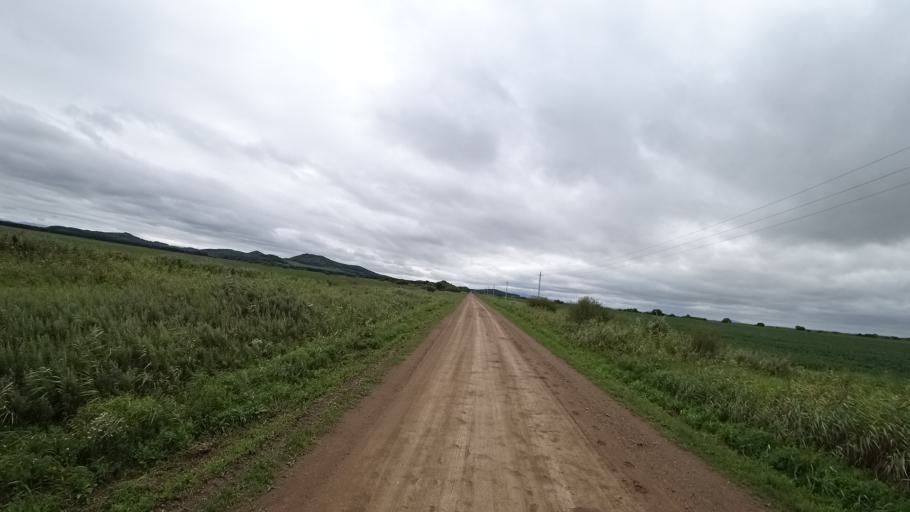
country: RU
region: Primorskiy
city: Chernigovka
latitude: 44.4936
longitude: 132.5713
